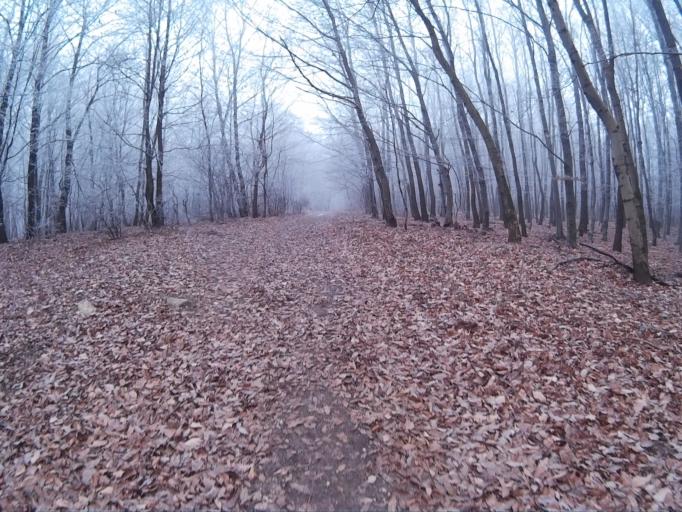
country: HU
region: Komarom-Esztergom
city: Oroszlany
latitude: 47.4431
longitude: 18.3679
